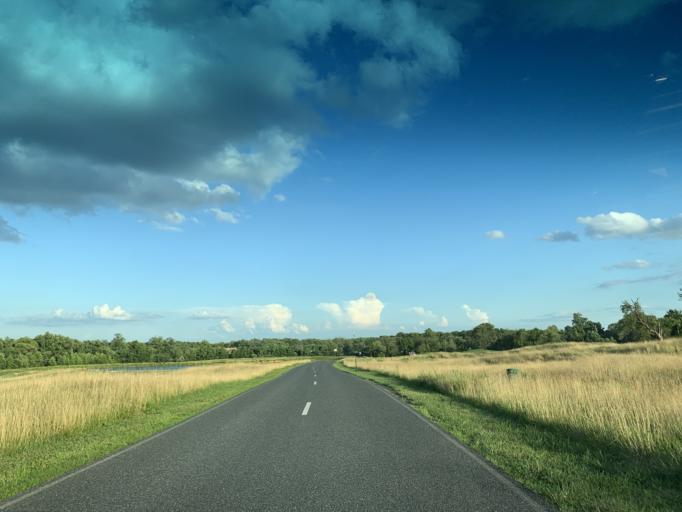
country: US
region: Maryland
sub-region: Harford County
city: Havre de Grace
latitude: 39.5361
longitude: -76.1291
